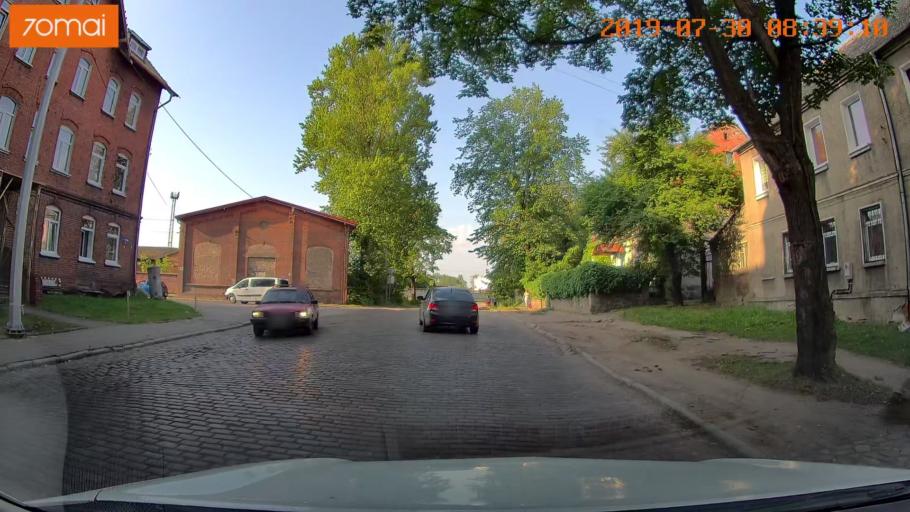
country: RU
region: Kaliningrad
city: Chernyakhovsk
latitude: 54.6316
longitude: 21.8025
